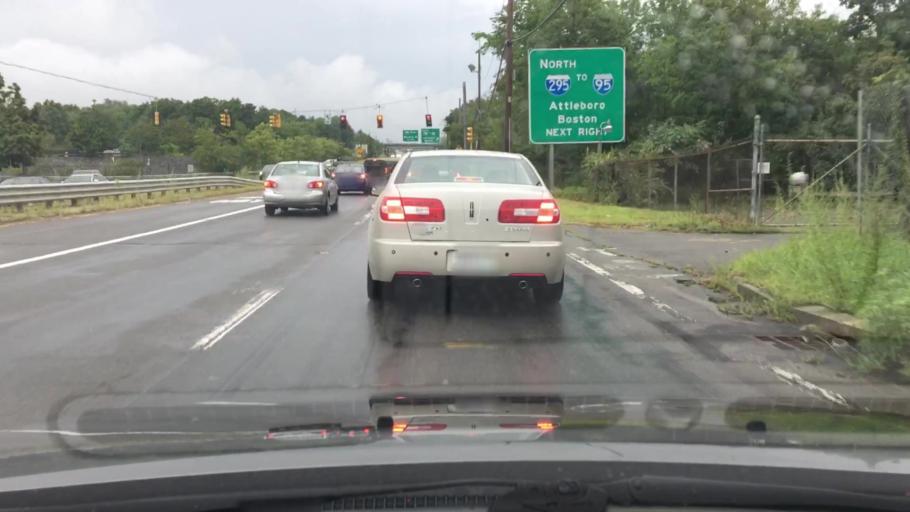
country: US
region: Rhode Island
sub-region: Providence County
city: Valley Falls
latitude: 41.9447
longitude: -71.3475
